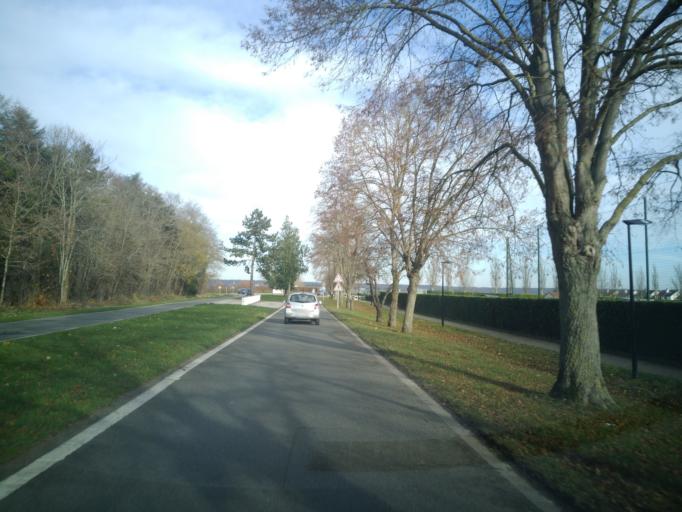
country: FR
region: Ile-de-France
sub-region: Departement des Yvelines
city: Villepreux
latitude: 48.8331
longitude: 2.0014
